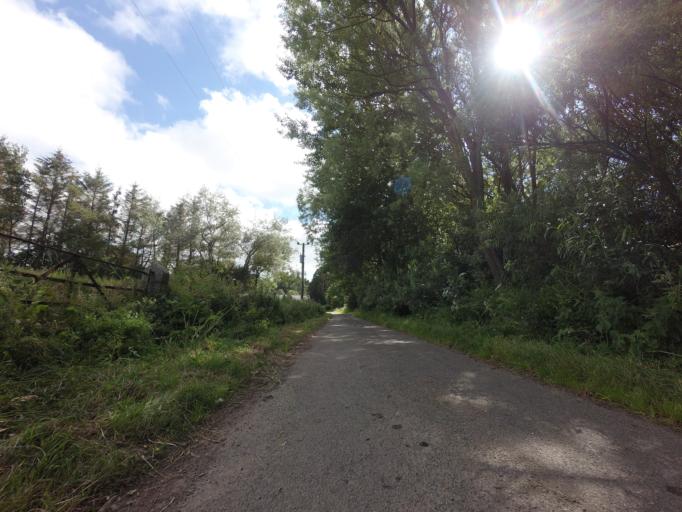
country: GB
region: Scotland
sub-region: Aberdeenshire
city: Banff
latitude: 57.6084
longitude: -2.5120
